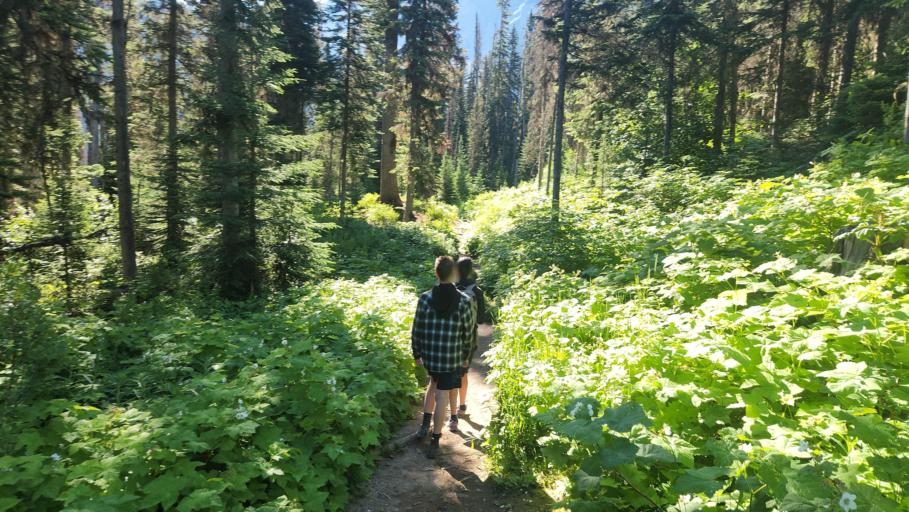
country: CA
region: Alberta
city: Lake Louise
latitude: 51.4383
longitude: -116.5341
